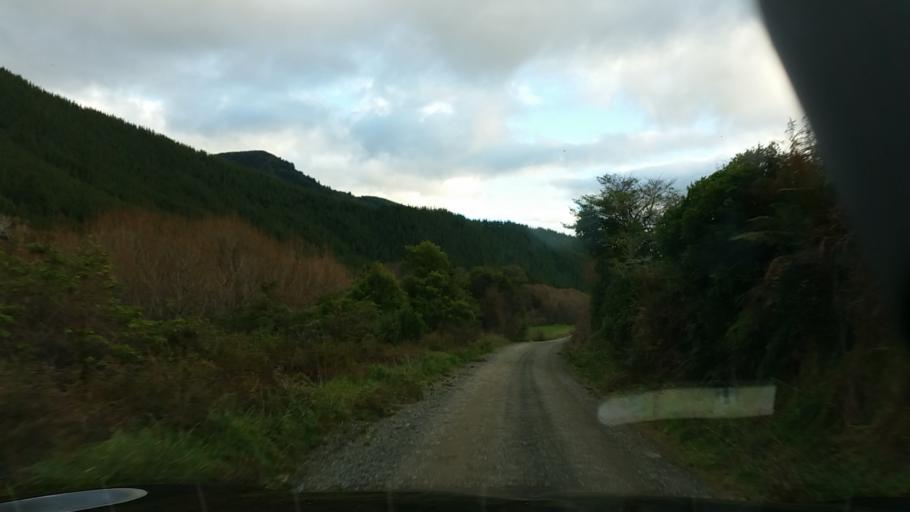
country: NZ
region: Nelson
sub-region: Nelson City
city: Nelson
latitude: -41.2096
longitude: 173.6324
